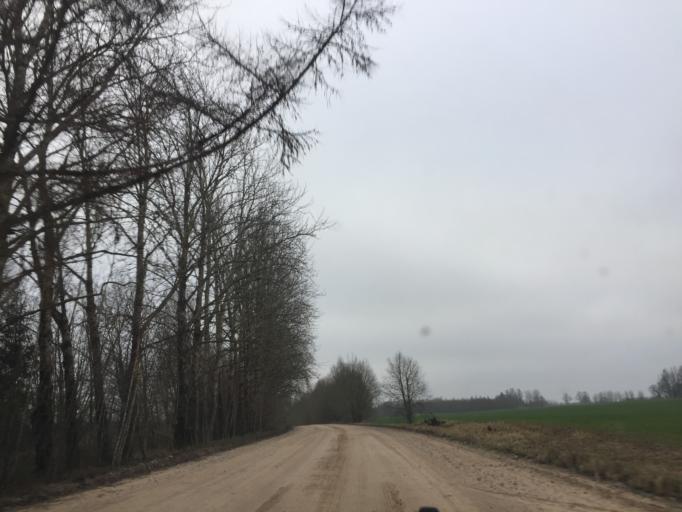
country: LV
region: Limbazu Rajons
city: Limbazi
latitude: 57.5981
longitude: 24.6159
